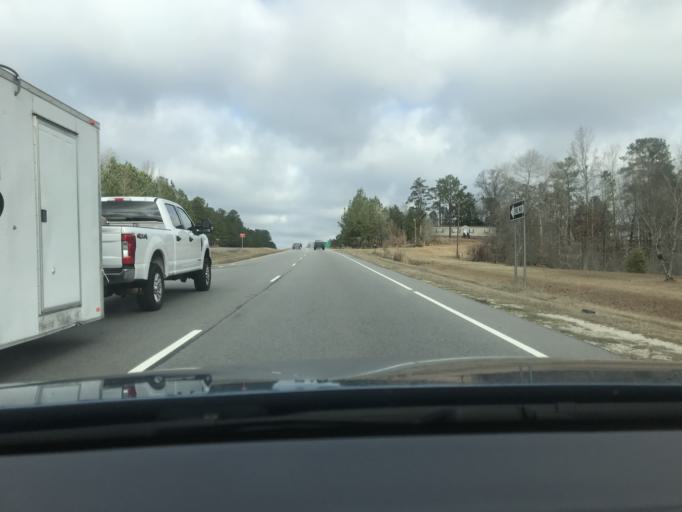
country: US
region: North Carolina
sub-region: Cumberland County
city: Spring Lake
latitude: 35.2882
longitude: -79.0764
